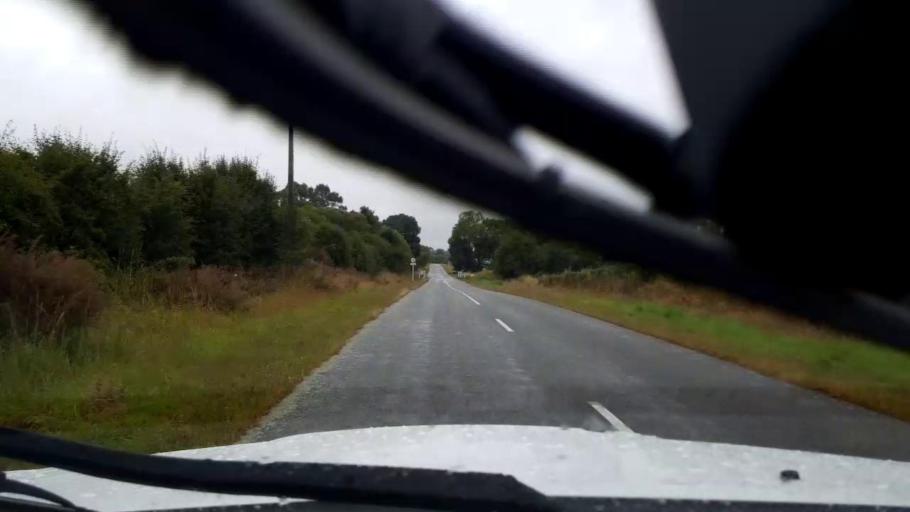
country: NZ
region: Canterbury
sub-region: Timaru District
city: Pleasant Point
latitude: -44.2525
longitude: 171.2547
